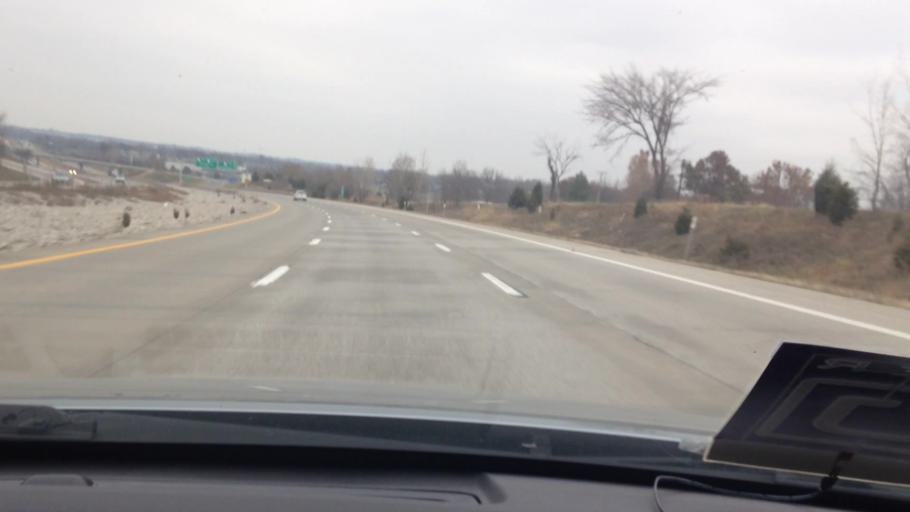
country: US
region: Missouri
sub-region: Cass County
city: Harrisonville
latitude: 38.6325
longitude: -94.3507
